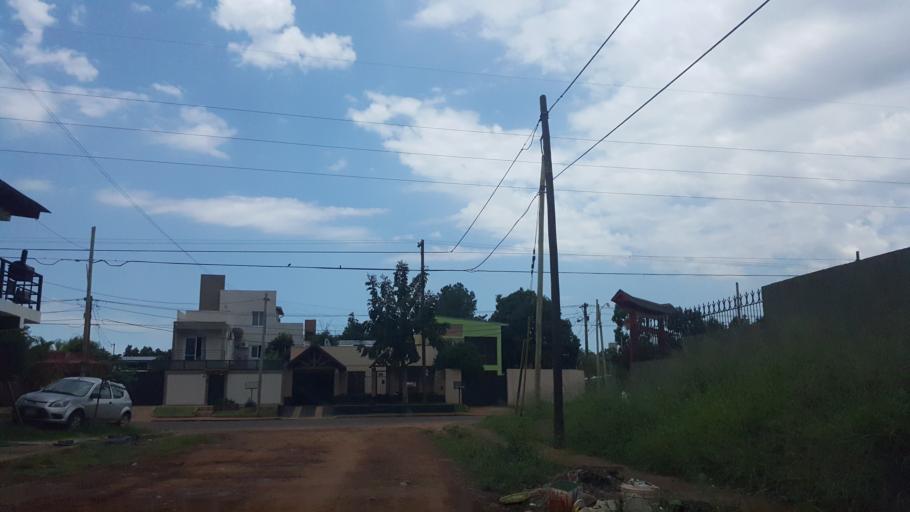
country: AR
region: Misiones
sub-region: Departamento de Capital
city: Posadas
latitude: -27.3753
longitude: -55.9158
